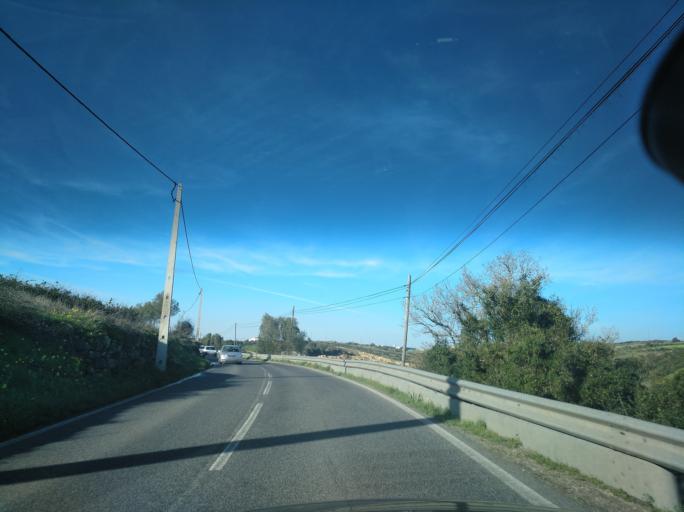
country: PT
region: Lisbon
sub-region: Mafra
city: Mafra
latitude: 38.9003
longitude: -9.3265
